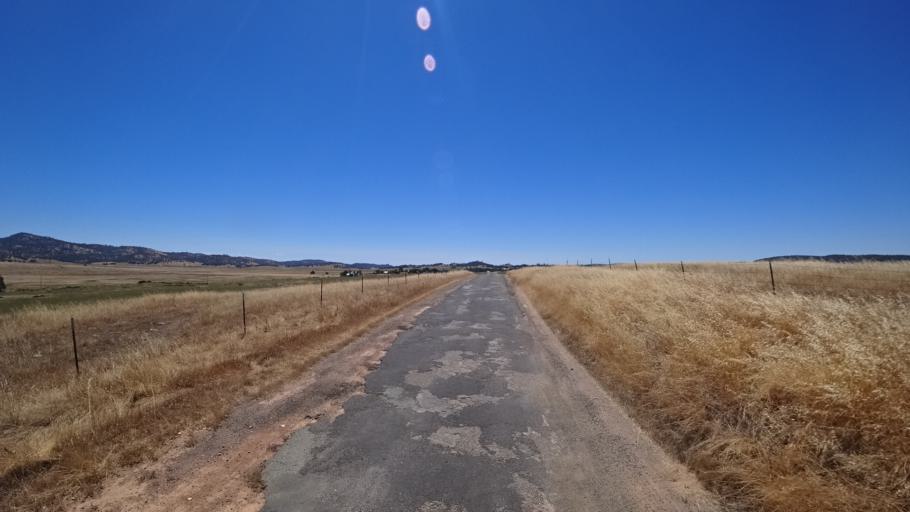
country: US
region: California
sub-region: Calaveras County
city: Copperopolis
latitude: 38.0429
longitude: -120.7306
